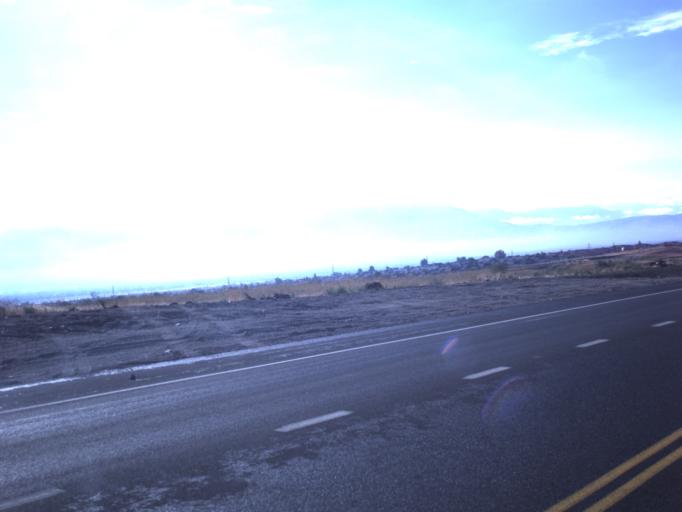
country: US
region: Utah
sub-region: Salt Lake County
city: Oquirrh
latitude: 40.6340
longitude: -112.0549
